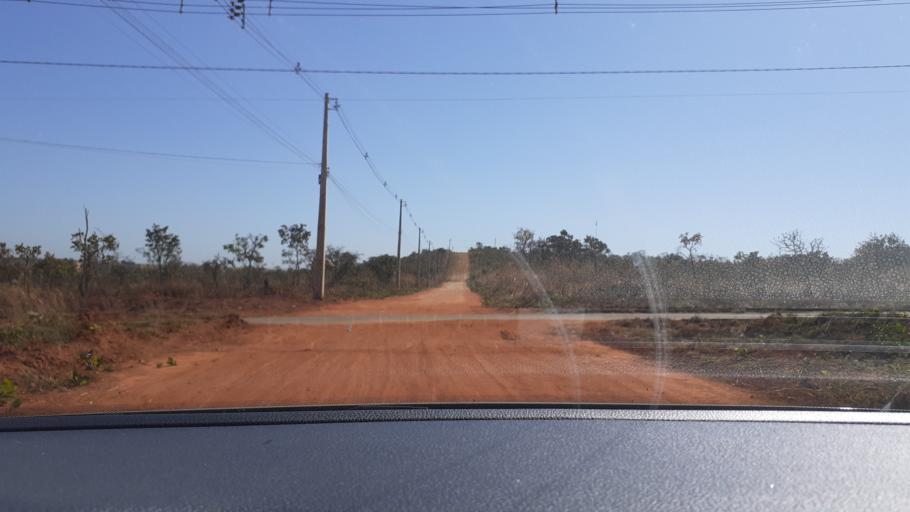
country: BR
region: Goias
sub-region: Aparecida De Goiania
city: Aparecida de Goiania
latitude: -16.8868
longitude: -49.2586
